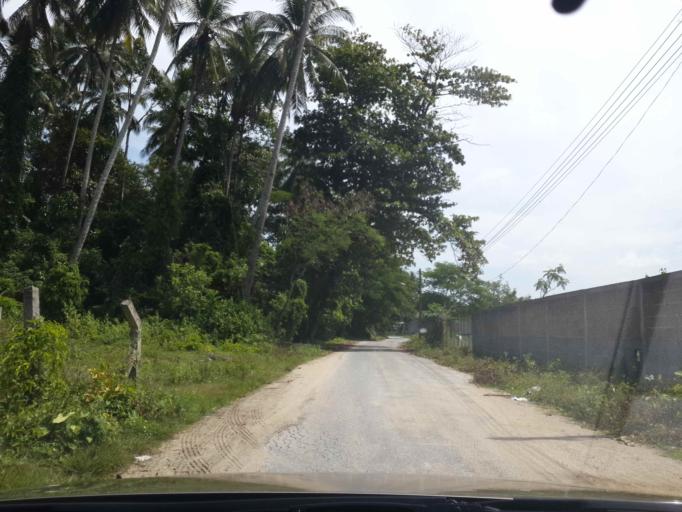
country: TH
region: Narathiwat
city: Rueso
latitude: 6.4037
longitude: 101.5170
